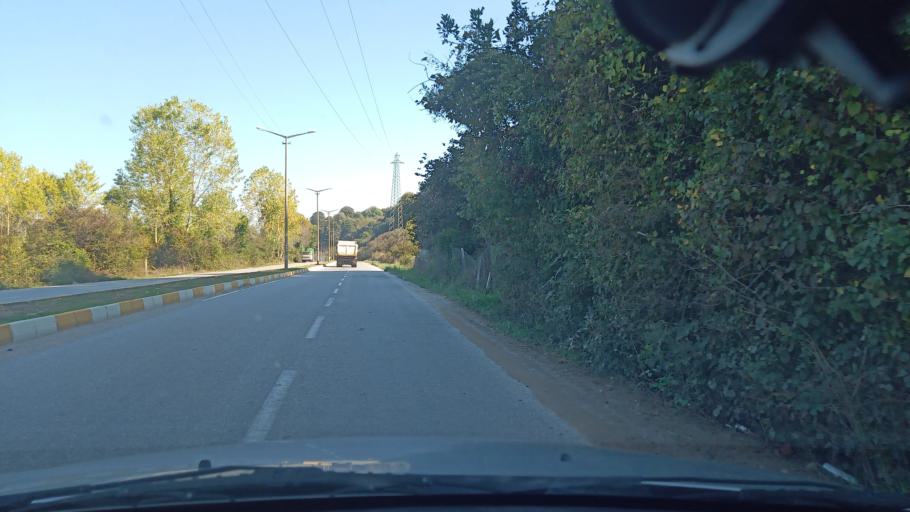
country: TR
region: Sakarya
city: Karasu
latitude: 41.1012
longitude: 30.6612
